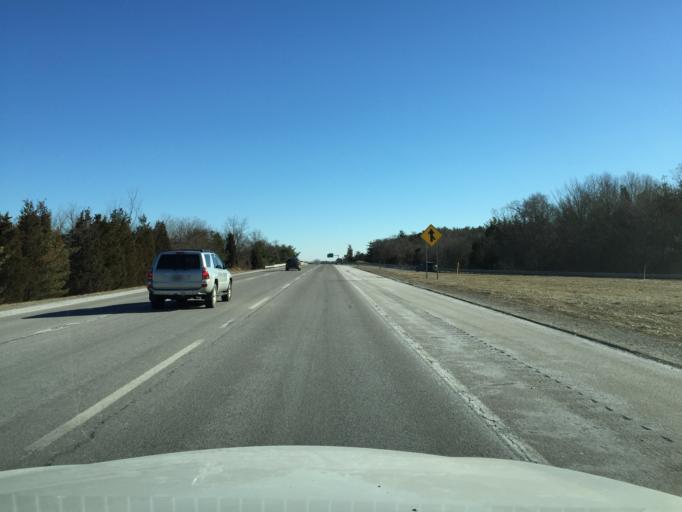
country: US
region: Massachusetts
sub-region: Norfolk County
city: Foxborough
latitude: 42.0280
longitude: -71.2607
